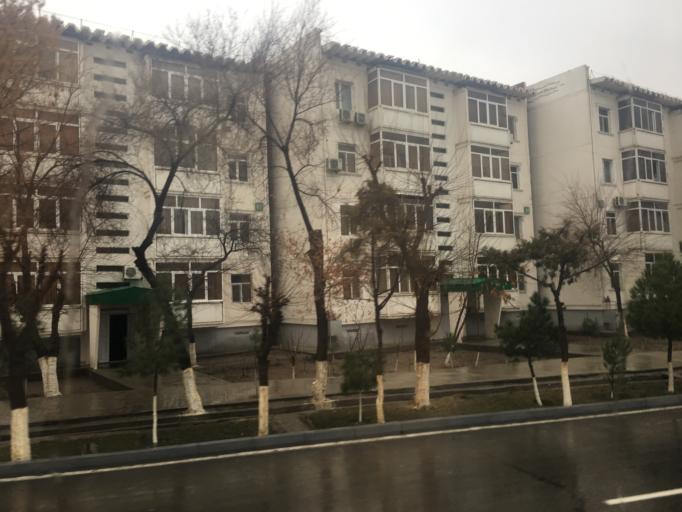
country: TM
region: Lebap
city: Turkmenabat
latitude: 39.0974
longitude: 63.5878
